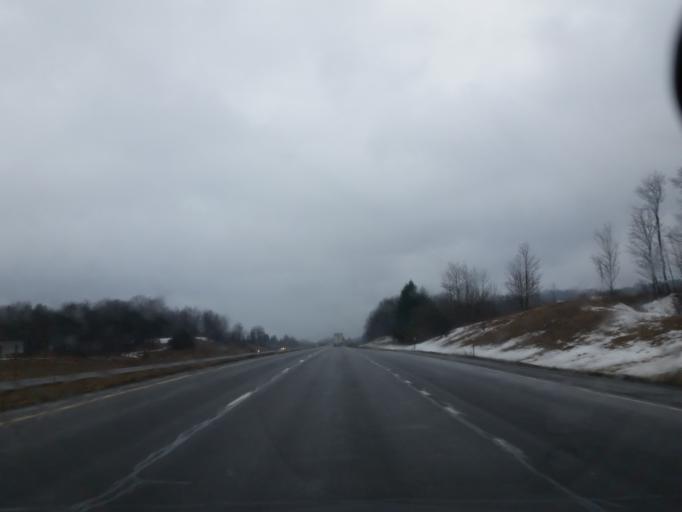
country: US
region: New York
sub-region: Chenango County
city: Lakeview
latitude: 42.3186
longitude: -75.9658
